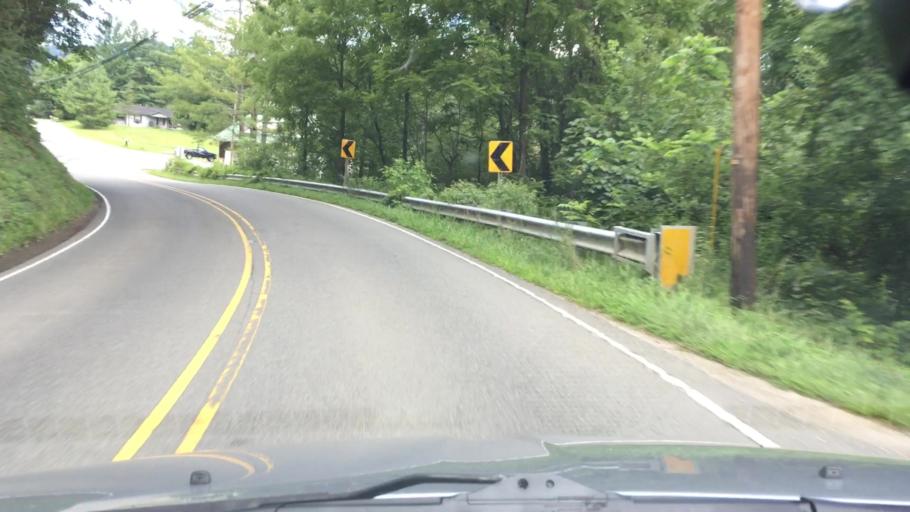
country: US
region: North Carolina
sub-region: Yancey County
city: Burnsville
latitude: 35.8440
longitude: -82.1900
